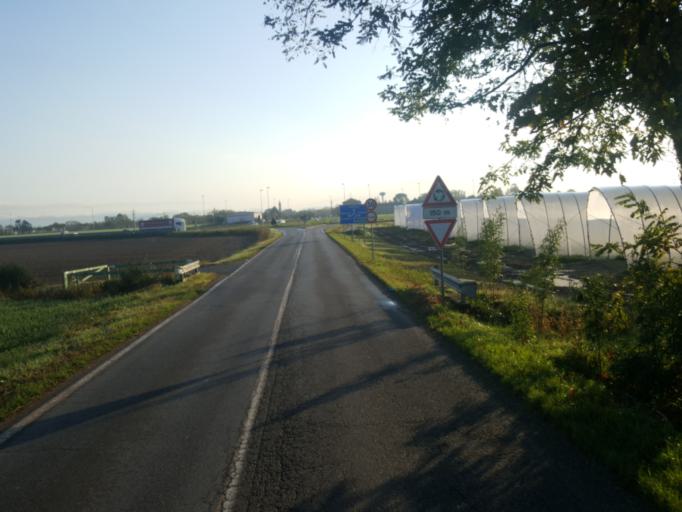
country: IT
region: Lombardy
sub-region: Provincia di Bergamo
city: Pagazzano
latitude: 45.5329
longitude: 9.6867
